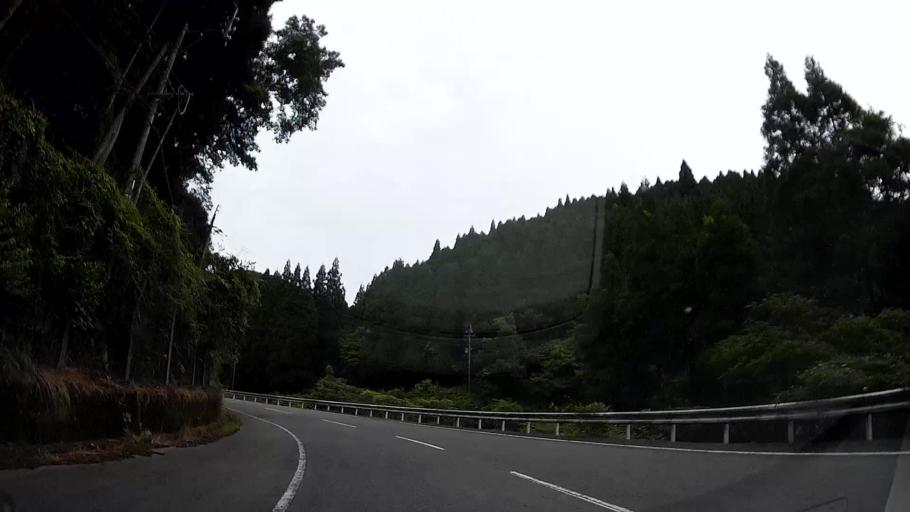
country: JP
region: Kumamoto
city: Kikuchi
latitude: 33.0468
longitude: 130.8967
